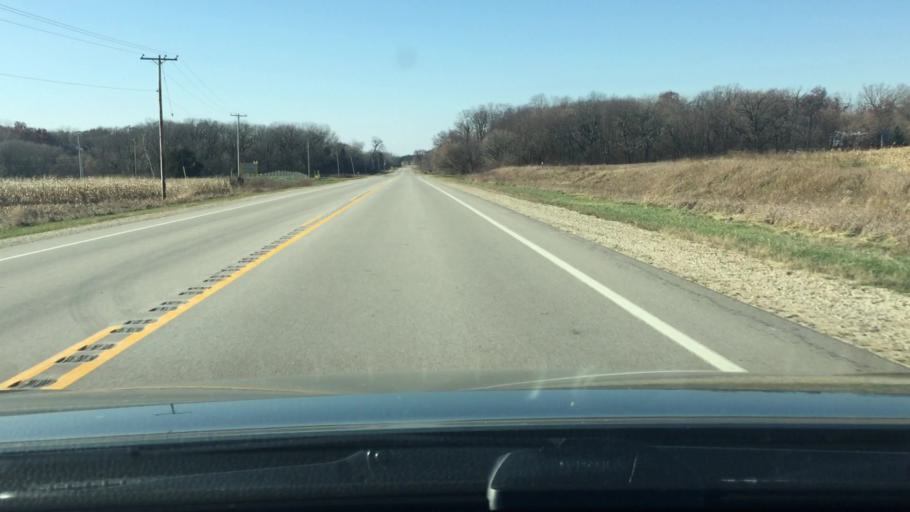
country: US
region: Wisconsin
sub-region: Jefferson County
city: Lake Ripley
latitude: 43.0077
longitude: -88.9329
